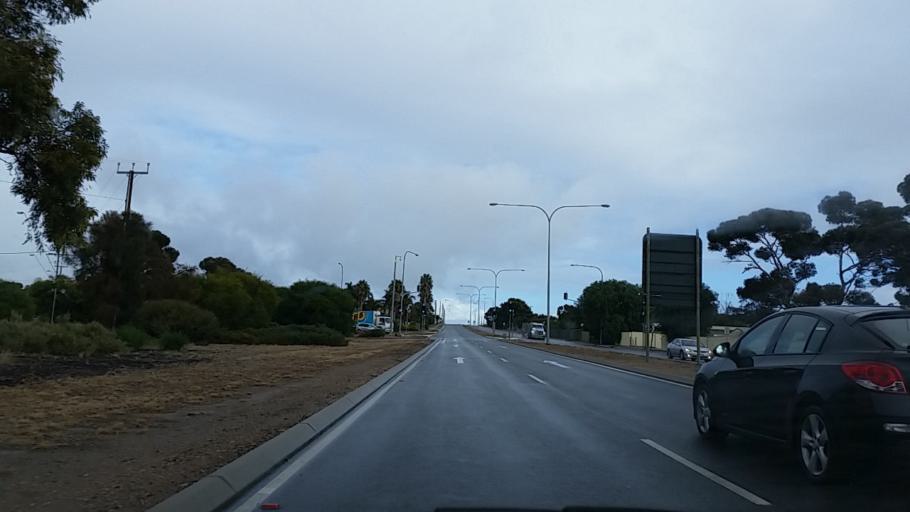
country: AU
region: South Australia
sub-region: Onkaparinga
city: Noarlunga
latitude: -35.1820
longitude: 138.4947
